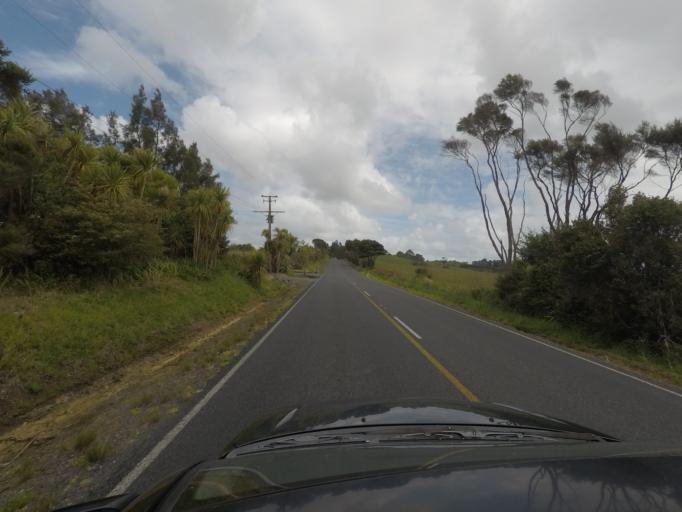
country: NZ
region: Auckland
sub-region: Auckland
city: Parakai
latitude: -36.6328
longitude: 174.5042
